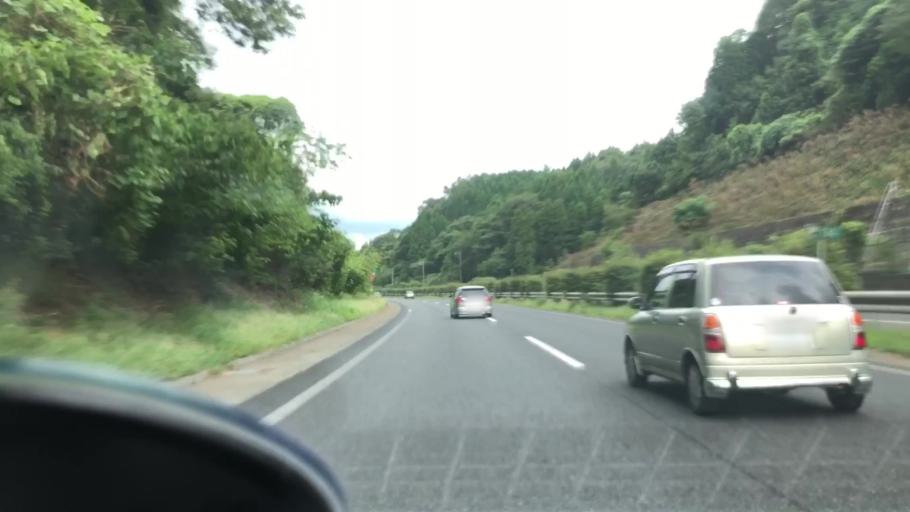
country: JP
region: Hyogo
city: Yamazakicho-nakabirose
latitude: 34.9830
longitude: 134.6093
